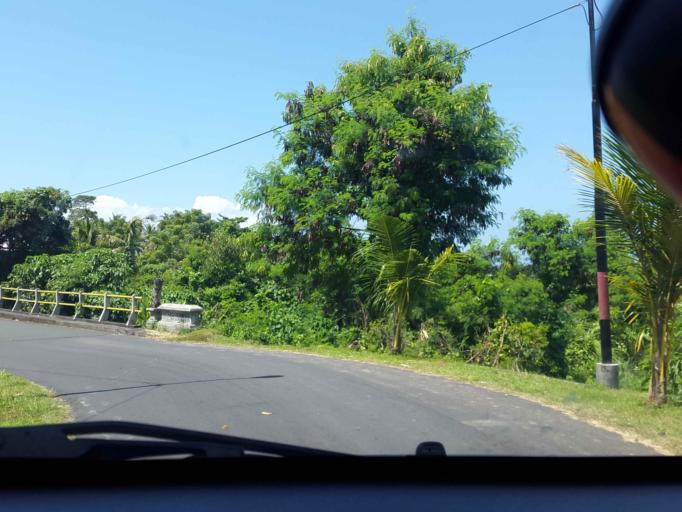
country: ID
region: Bali
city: Klungkung
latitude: -8.5357
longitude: 115.3928
